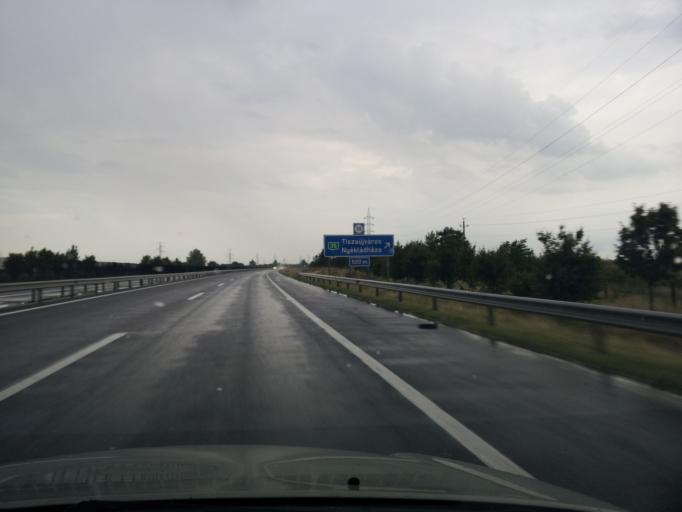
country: HU
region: Borsod-Abauj-Zemplen
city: Onod
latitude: 47.9919
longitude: 20.8939
